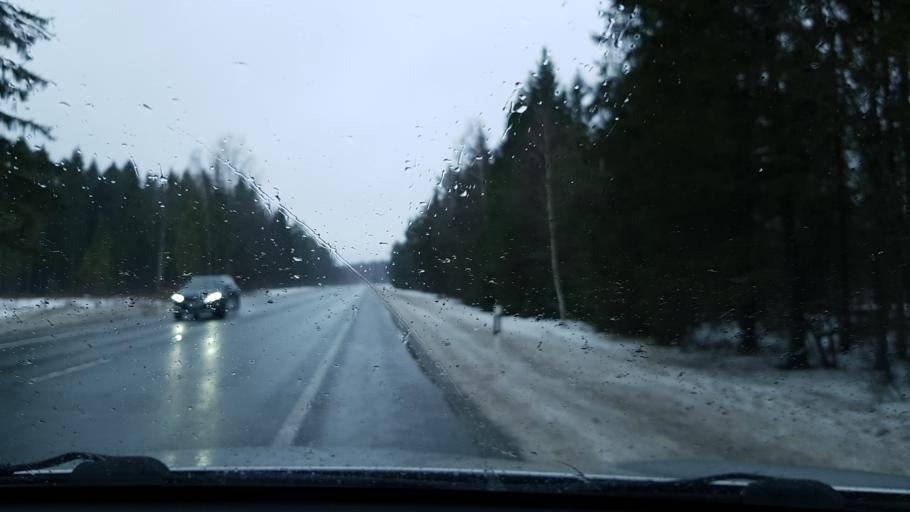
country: EE
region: Raplamaa
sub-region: Kohila vald
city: Kohila
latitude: 59.1573
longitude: 24.7763
